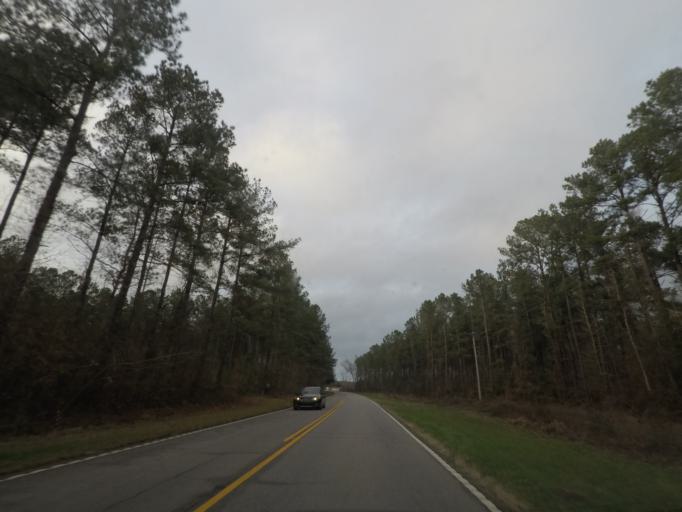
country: US
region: South Carolina
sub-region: Dorchester County
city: Saint George
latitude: 33.0690
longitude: -80.6330
